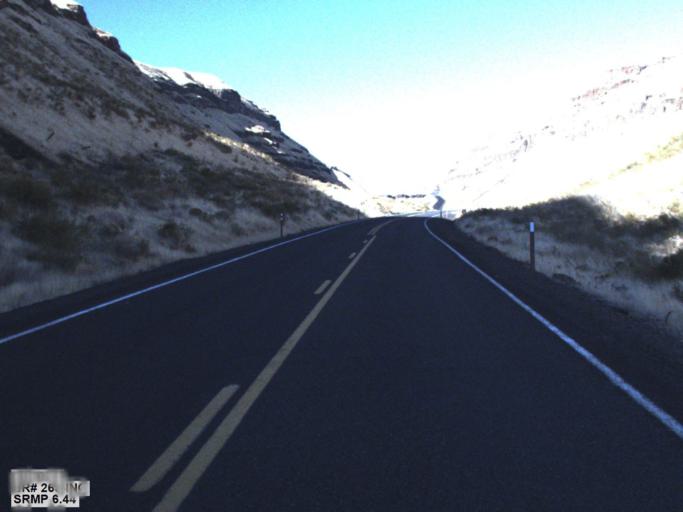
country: US
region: Washington
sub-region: Franklin County
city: Connell
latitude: 46.6069
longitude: -118.5526
